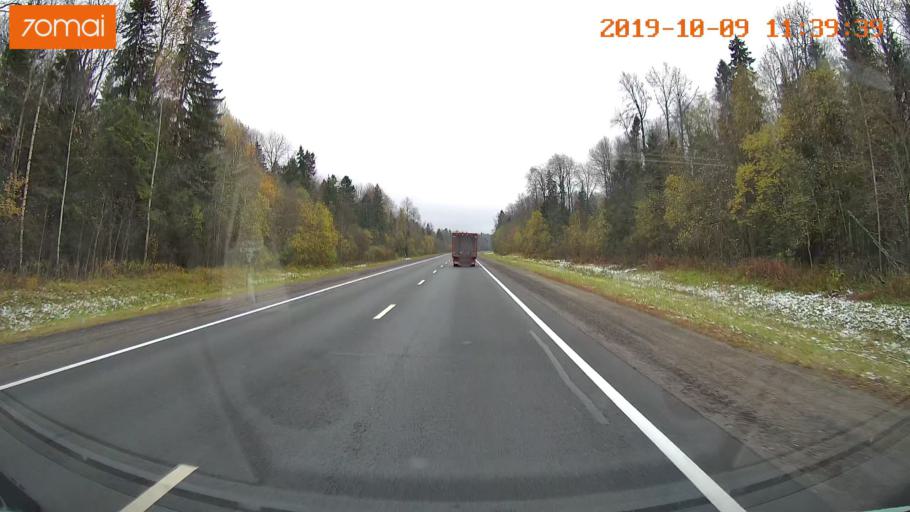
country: RU
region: Vologda
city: Gryazovets
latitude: 58.9535
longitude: 40.1680
